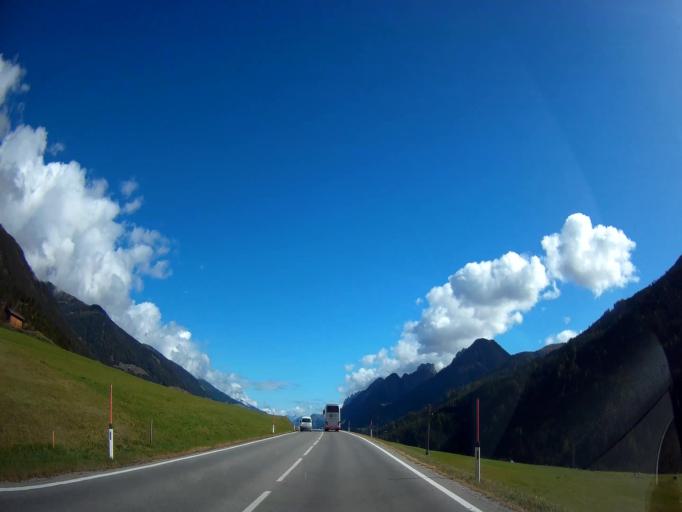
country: AT
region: Tyrol
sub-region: Politischer Bezirk Lienz
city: Strassen
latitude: 46.7496
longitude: 12.4933
